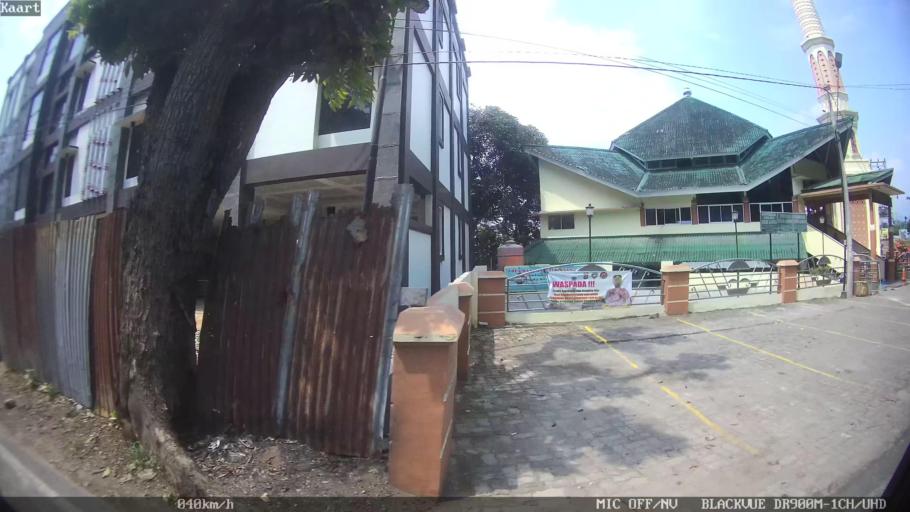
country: ID
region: Lampung
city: Bandarlampung
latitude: -5.4292
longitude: 105.2542
